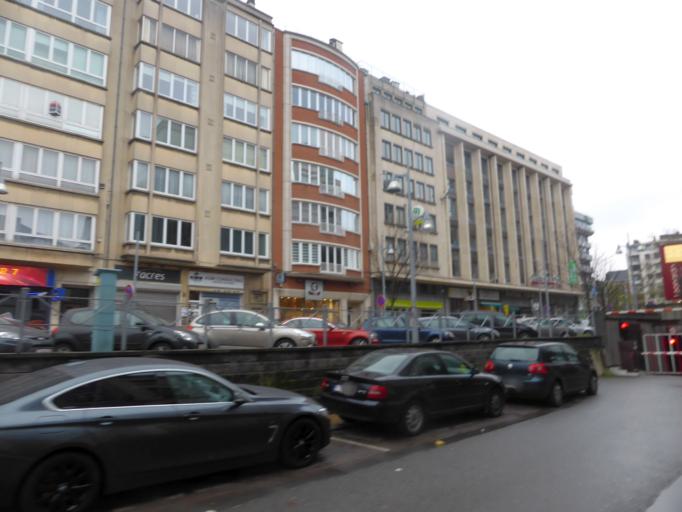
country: BE
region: Wallonia
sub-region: Province du Hainaut
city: Charleroi
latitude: 50.4079
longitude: 4.4441
